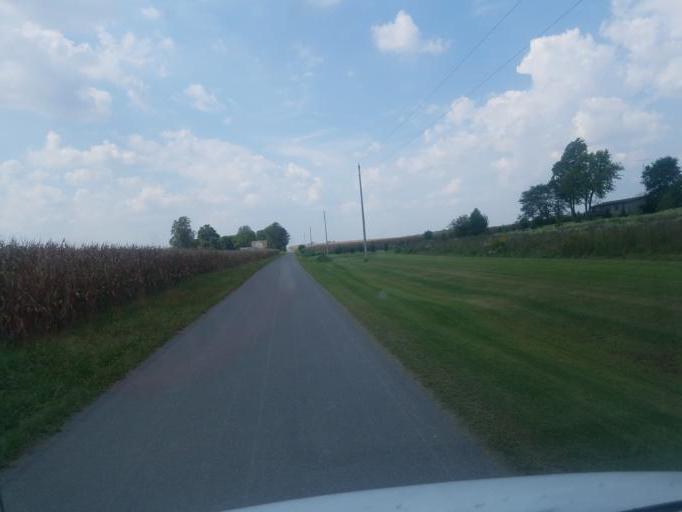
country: US
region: Ohio
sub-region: Hardin County
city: Ada
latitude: 40.6377
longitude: -83.8726
